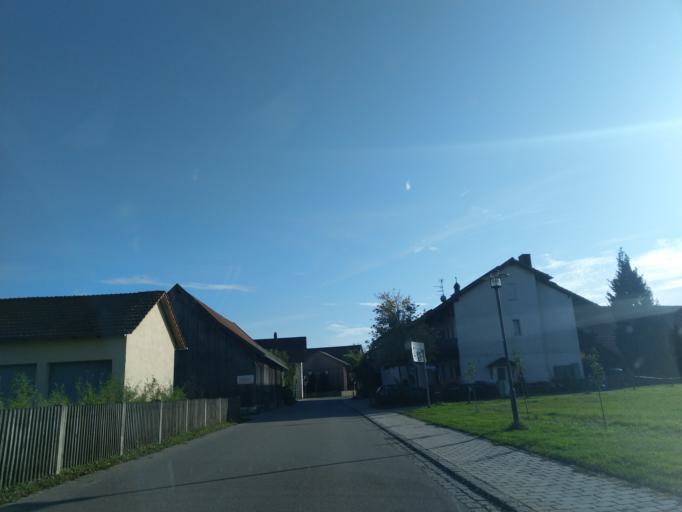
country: DE
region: Bavaria
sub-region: Lower Bavaria
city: Metten
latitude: 48.8632
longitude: 12.8933
